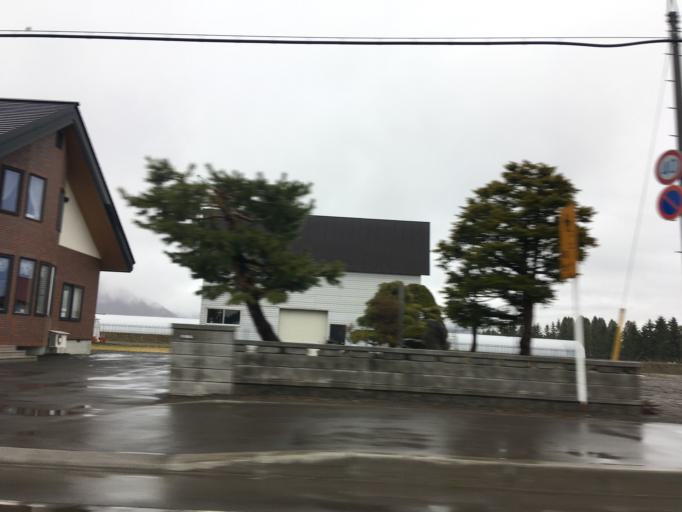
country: JP
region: Hokkaido
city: Nayoro
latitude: 44.1323
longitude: 142.4859
